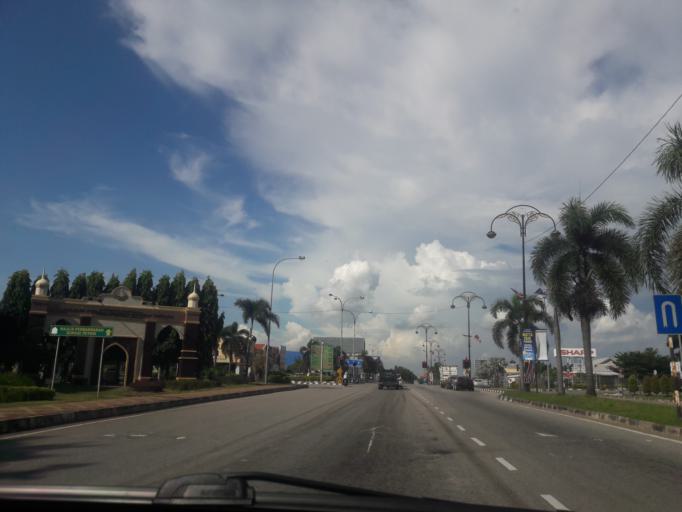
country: MY
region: Kedah
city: Sungai Petani
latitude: 5.6197
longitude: 100.4740
